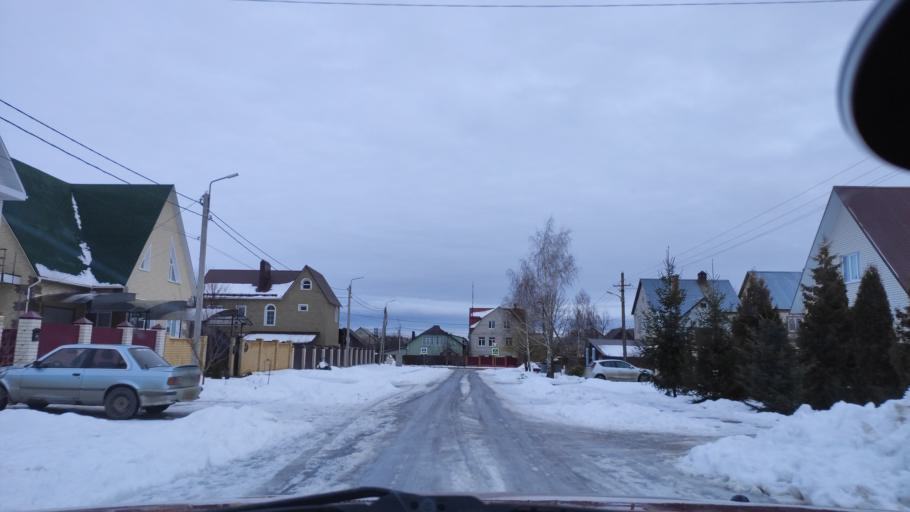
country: RU
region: Tambov
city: Tambov
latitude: 52.7625
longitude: 41.3744
